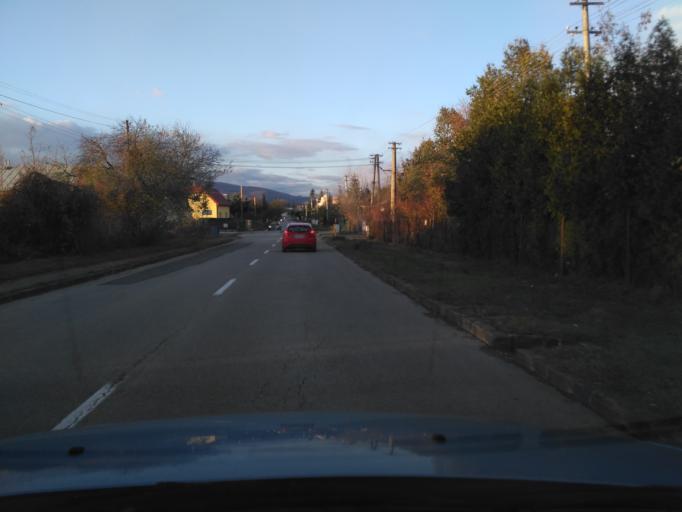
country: SK
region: Kosicky
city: Secovce
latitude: 48.6903
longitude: 21.6536
